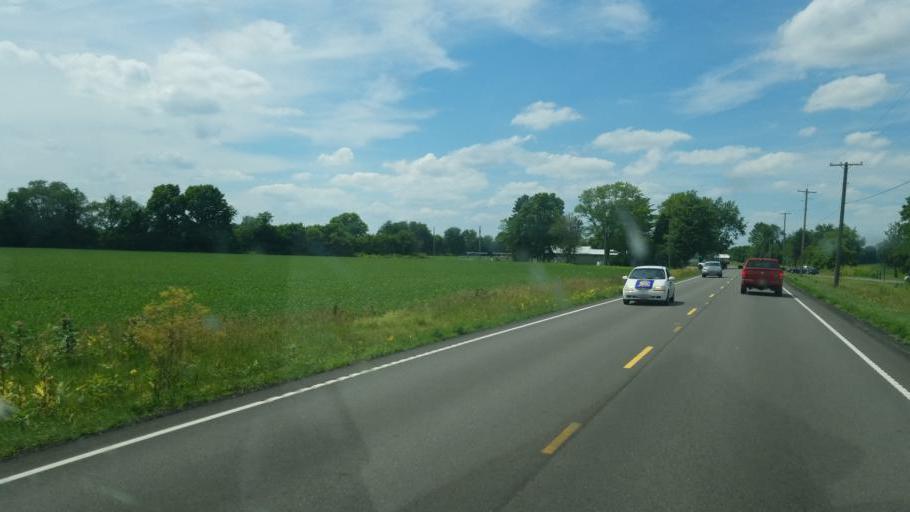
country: US
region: Ohio
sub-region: Knox County
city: Fredericktown
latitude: 40.4389
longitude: -82.5216
